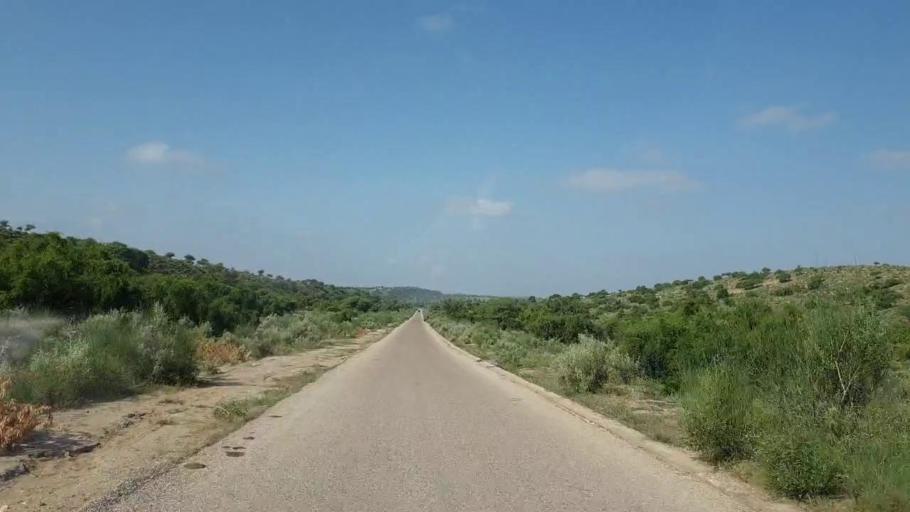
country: PK
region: Sindh
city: Mithi
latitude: 24.5608
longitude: 69.9048
